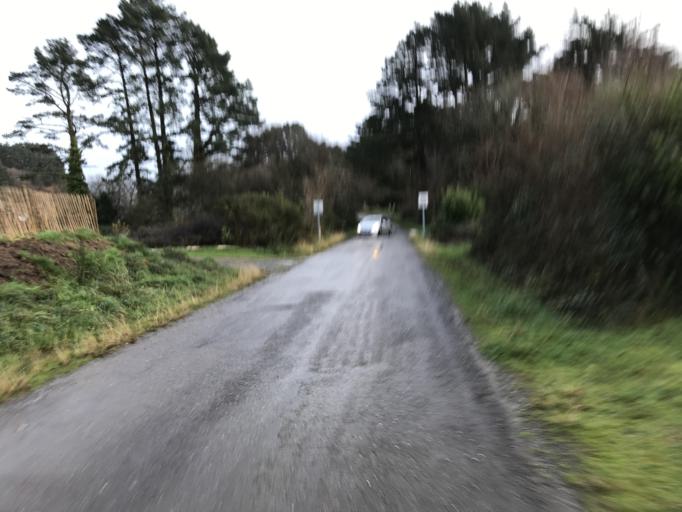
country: FR
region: Brittany
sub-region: Departement du Finistere
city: Logonna-Daoulas
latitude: 48.3176
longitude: -4.3122
